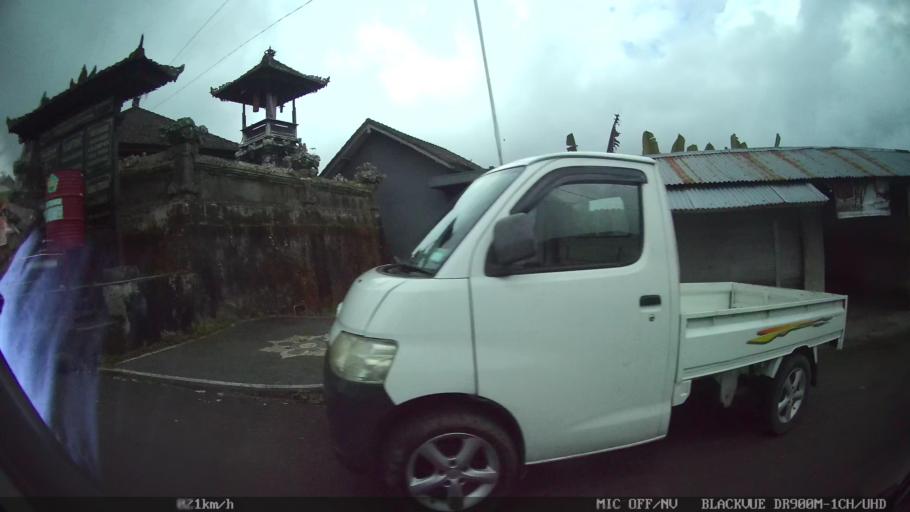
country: ID
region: Bali
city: Peneng
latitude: -8.3501
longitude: 115.2065
